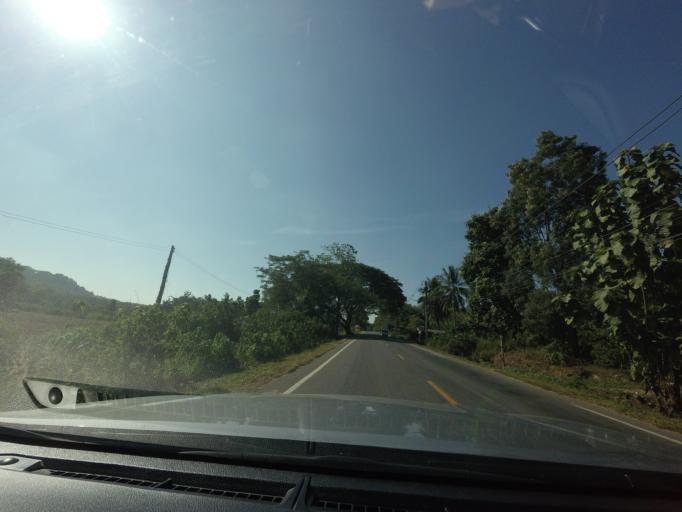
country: TH
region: Sukhothai
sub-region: Amphoe Si Satchanalai
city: Si Satchanalai
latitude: 17.6312
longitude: 99.6960
